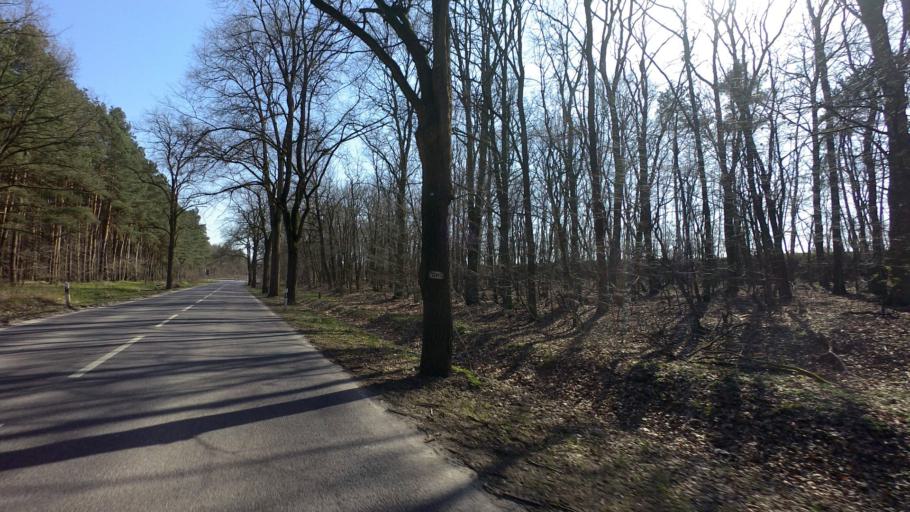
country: DE
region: Brandenburg
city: Leegebruch
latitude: 52.7383
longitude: 13.1780
